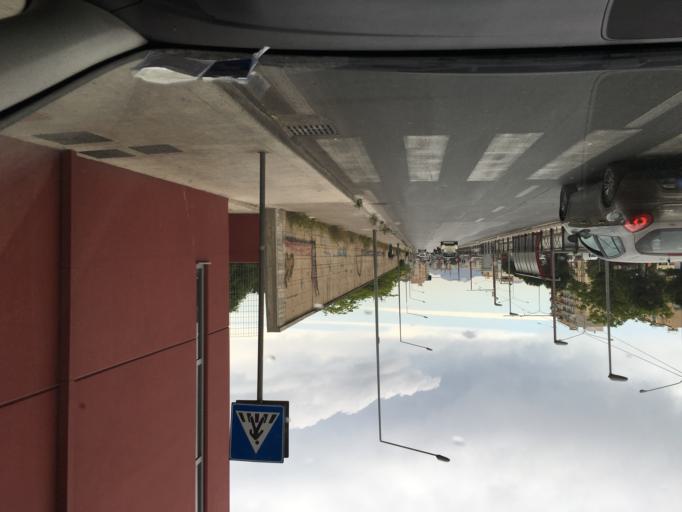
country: IT
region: Sicily
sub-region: Palermo
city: Palermo
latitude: 38.1070
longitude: 13.3304
